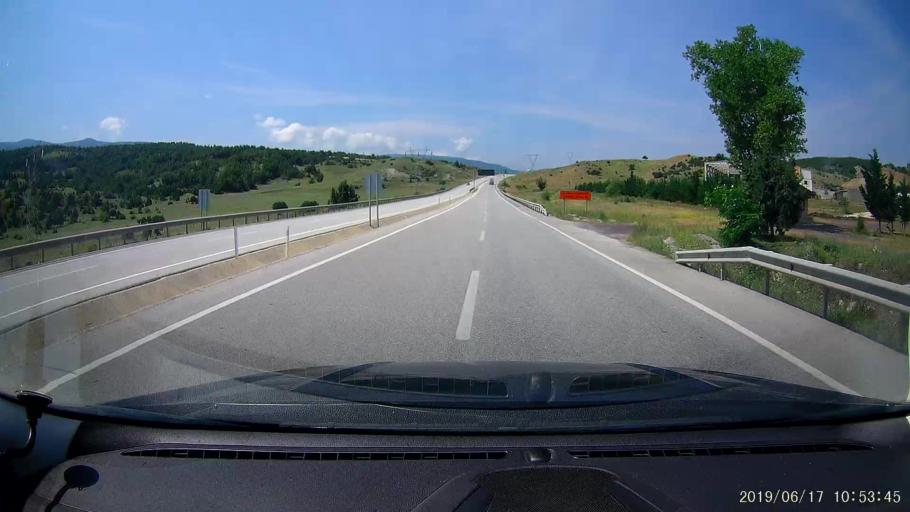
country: TR
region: Corum
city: Hacihamza
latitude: 41.0797
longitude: 34.3146
